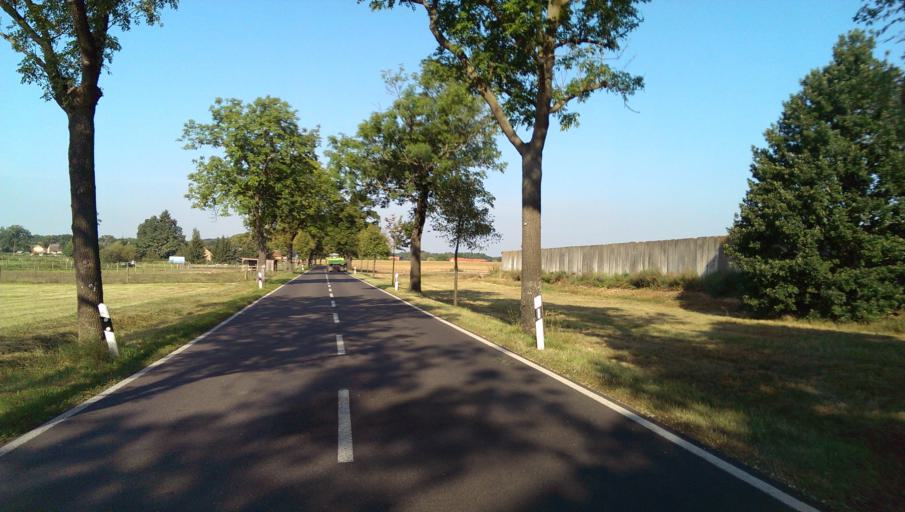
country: DE
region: Brandenburg
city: Luckenwalde
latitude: 52.1642
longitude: 13.0735
